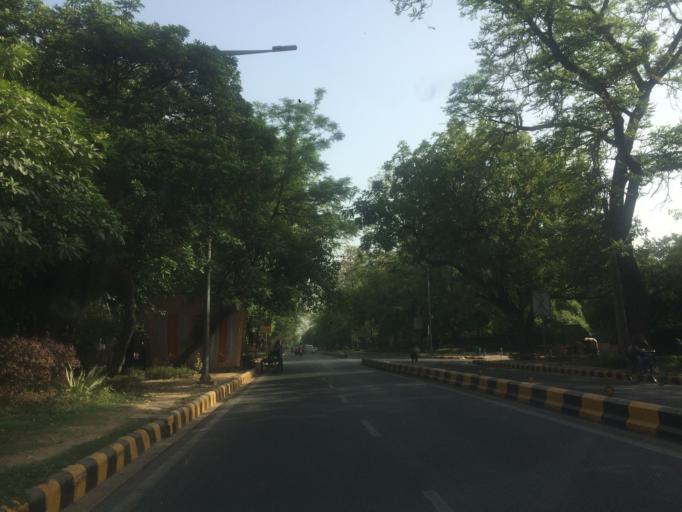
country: IN
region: NCT
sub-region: New Delhi
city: New Delhi
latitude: 28.6172
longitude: 77.2314
